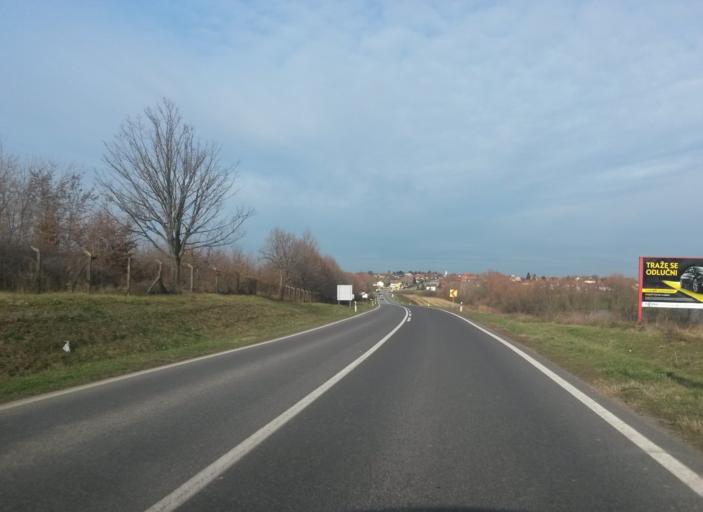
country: HR
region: Osjecko-Baranjska
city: Viskovci
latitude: 45.3386
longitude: 18.4210
